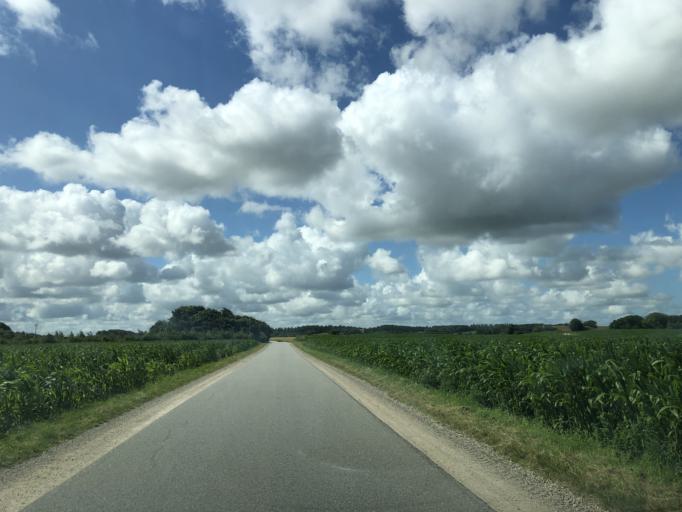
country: DK
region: Central Jutland
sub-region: Struer Kommune
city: Struer
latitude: 56.4450
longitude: 8.5165
